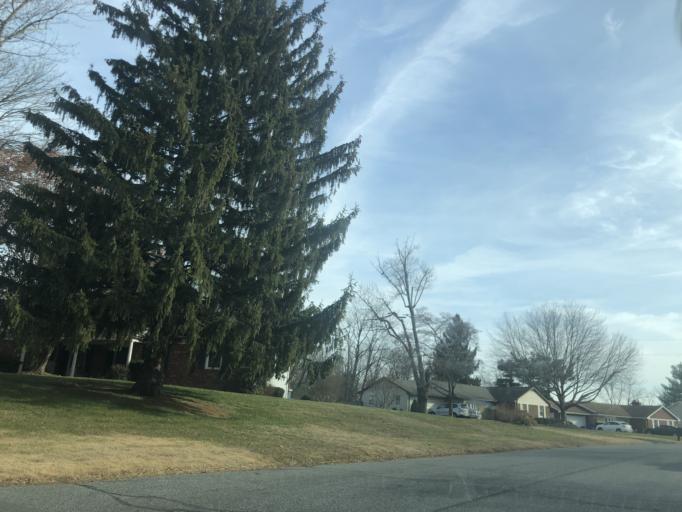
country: US
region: Maryland
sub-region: Howard County
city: Columbia
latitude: 39.2870
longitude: -76.8505
